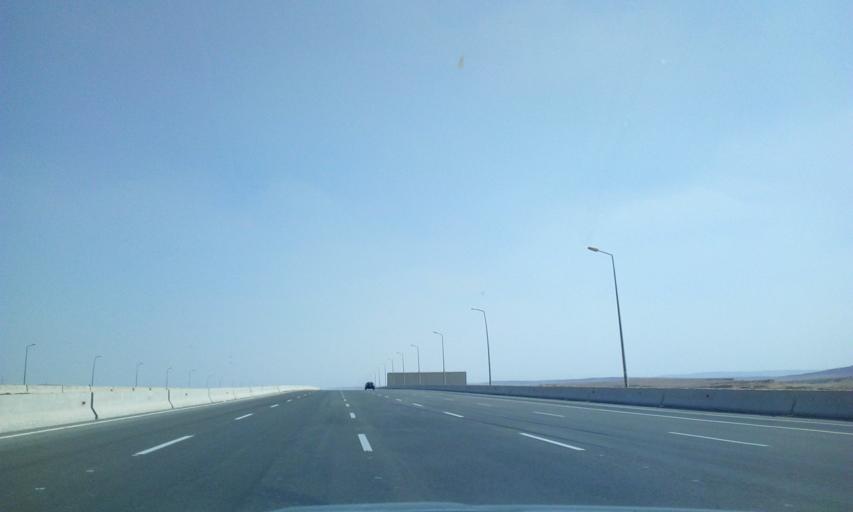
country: EG
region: As Suways
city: Ain Sukhna
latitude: 29.8387
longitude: 31.8779
